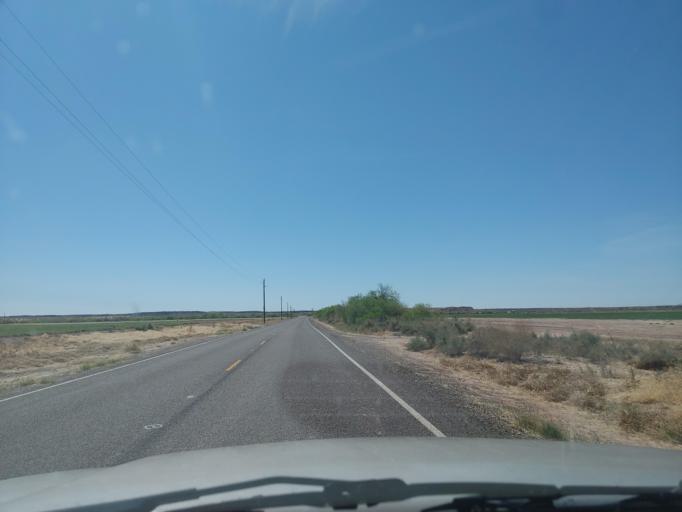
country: US
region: Arizona
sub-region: Maricopa County
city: Gila Bend
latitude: 32.9544
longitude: -113.3055
